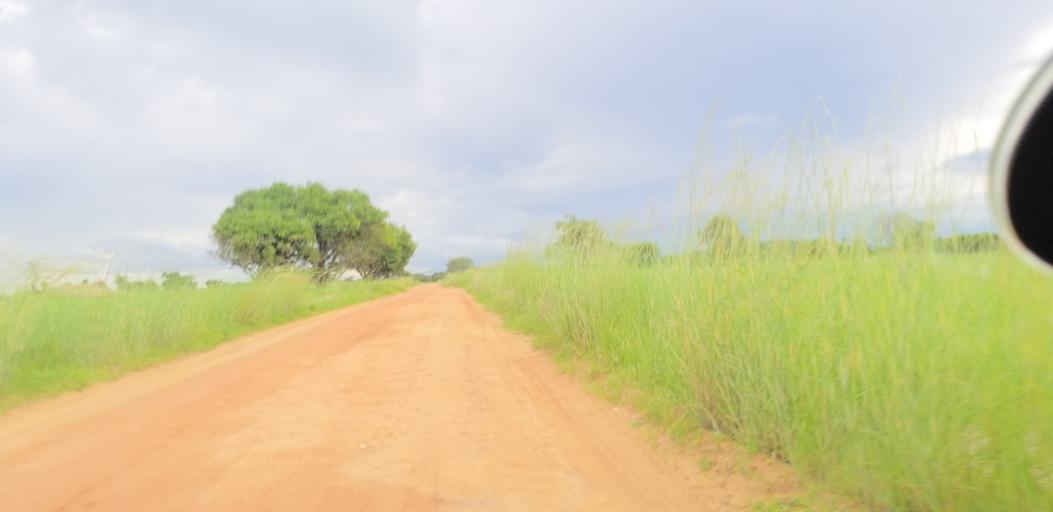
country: ZM
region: Lusaka
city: Chongwe
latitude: -15.1722
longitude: 28.4691
